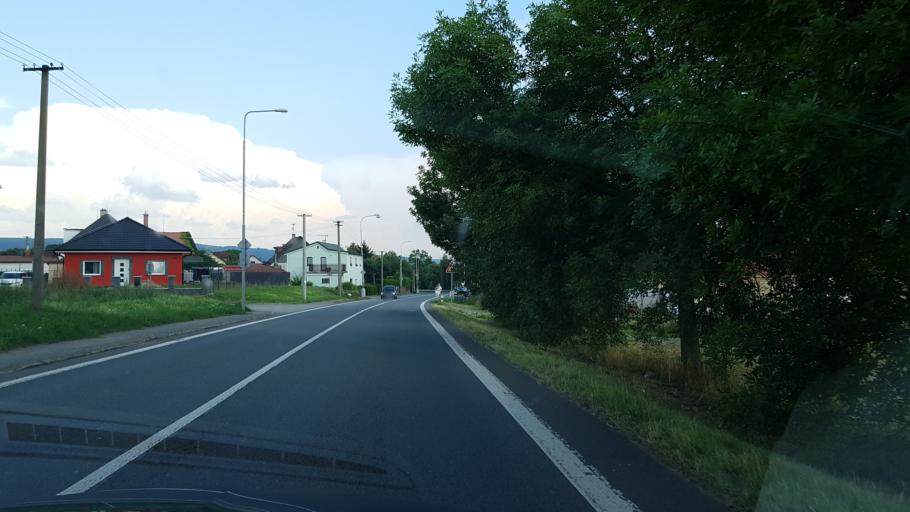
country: CZ
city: Doudleby nad Orlici
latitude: 50.1122
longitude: 16.2516
